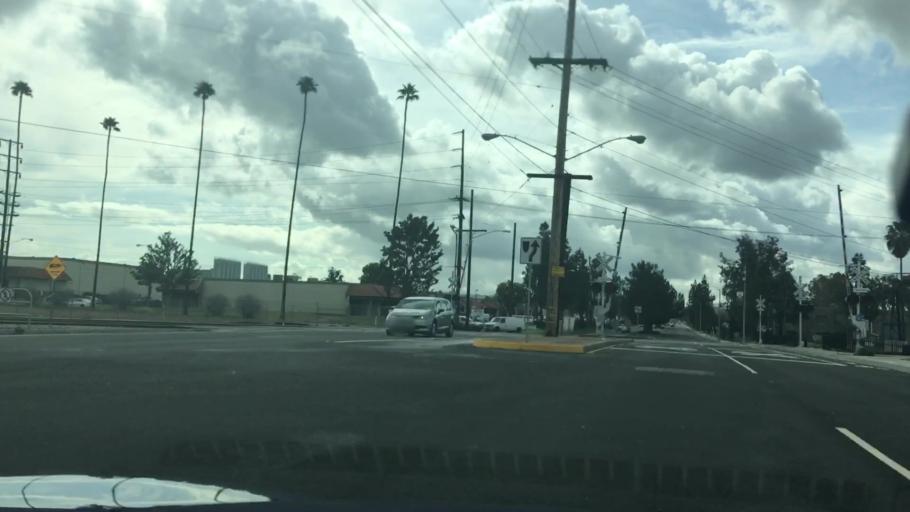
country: US
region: California
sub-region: Riverside County
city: Highgrove
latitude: 33.9984
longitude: -117.3485
